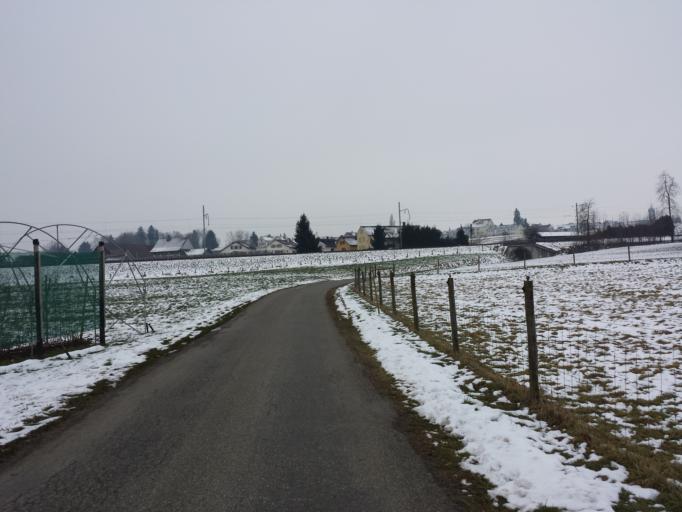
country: CH
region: Thurgau
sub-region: Arbon District
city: Egnach
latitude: 47.5363
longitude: 9.3710
